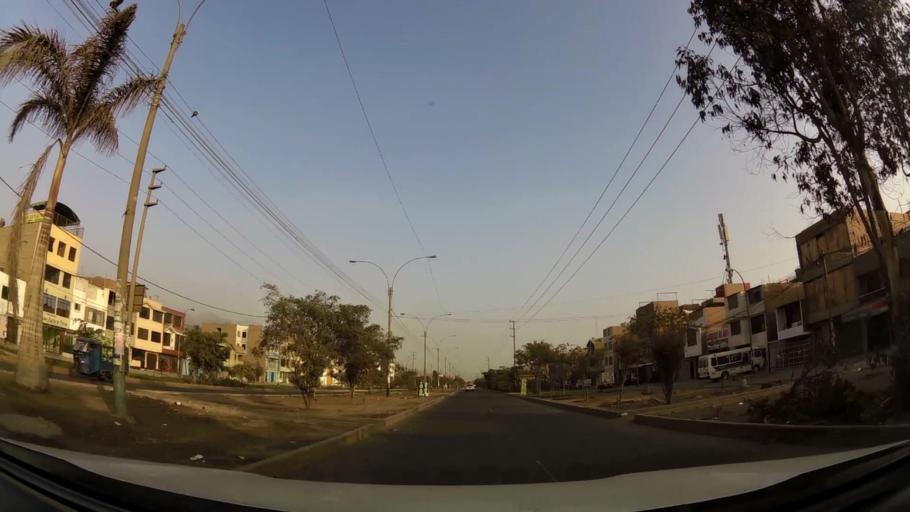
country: PE
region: Lima
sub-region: Lima
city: Independencia
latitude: -11.9572
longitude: -77.0637
